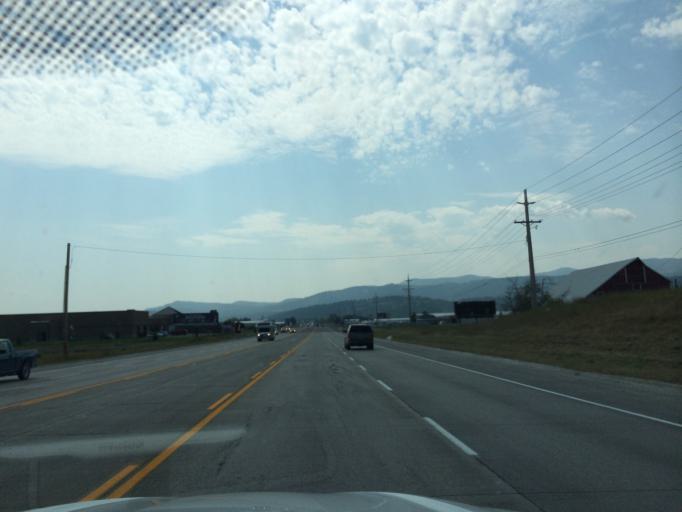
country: US
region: Montana
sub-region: Flathead County
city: Kalispell
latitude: 48.1605
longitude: -114.2878
